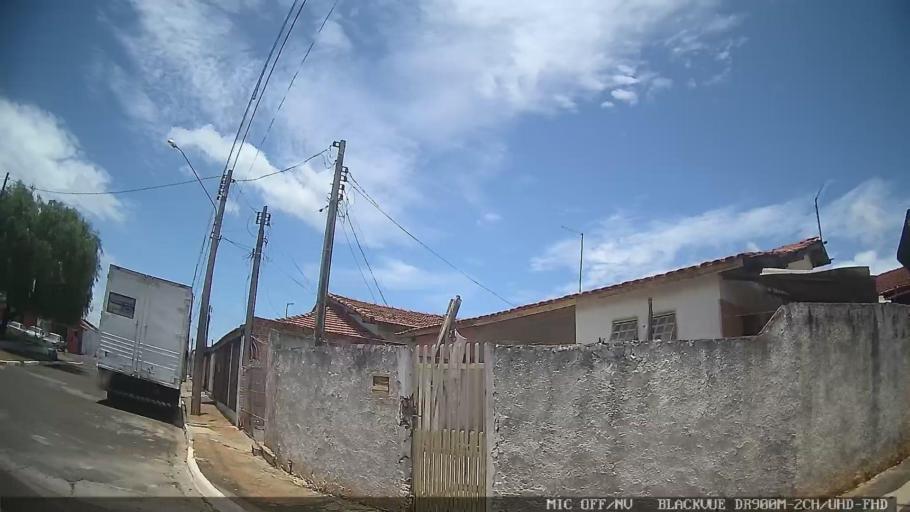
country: BR
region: Sao Paulo
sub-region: Laranjal Paulista
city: Laranjal Paulista
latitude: -23.0512
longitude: -47.8284
